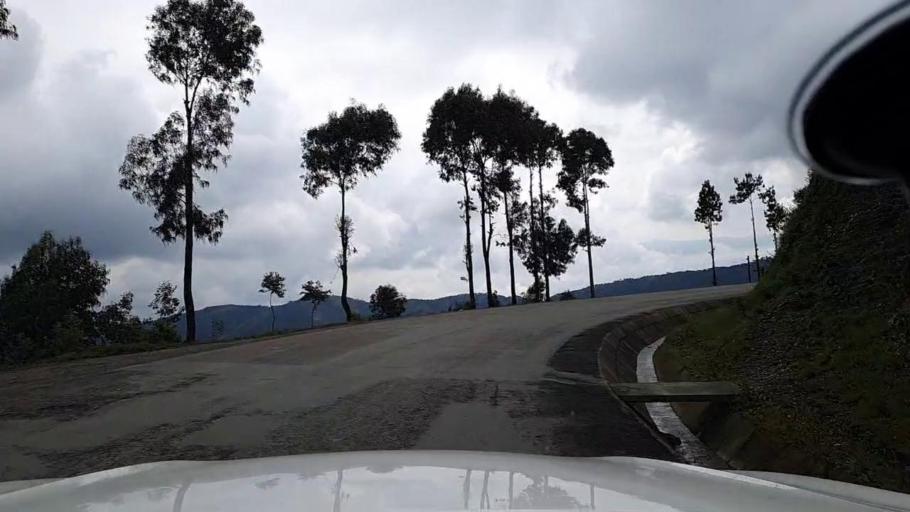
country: RW
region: Western Province
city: Kibuye
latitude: -2.0638
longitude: 29.5316
